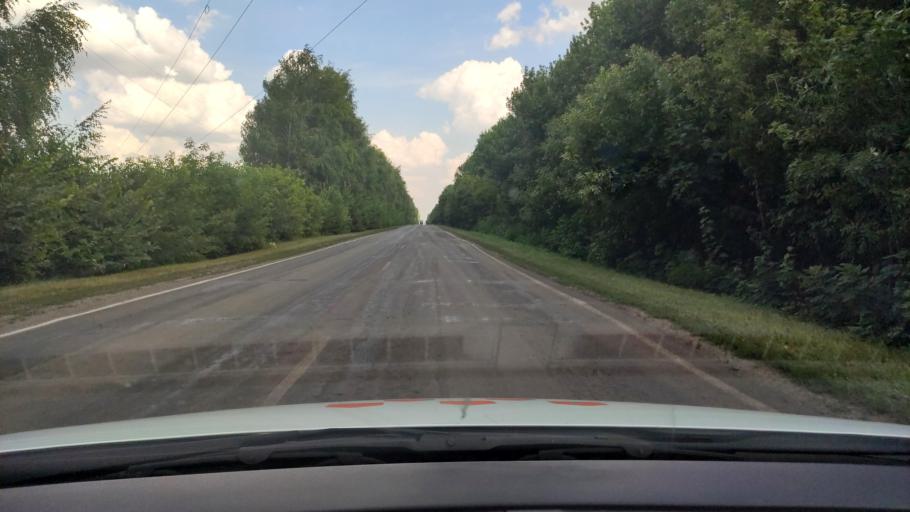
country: RU
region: Voronezj
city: Ertil'
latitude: 51.8065
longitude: 40.7711
